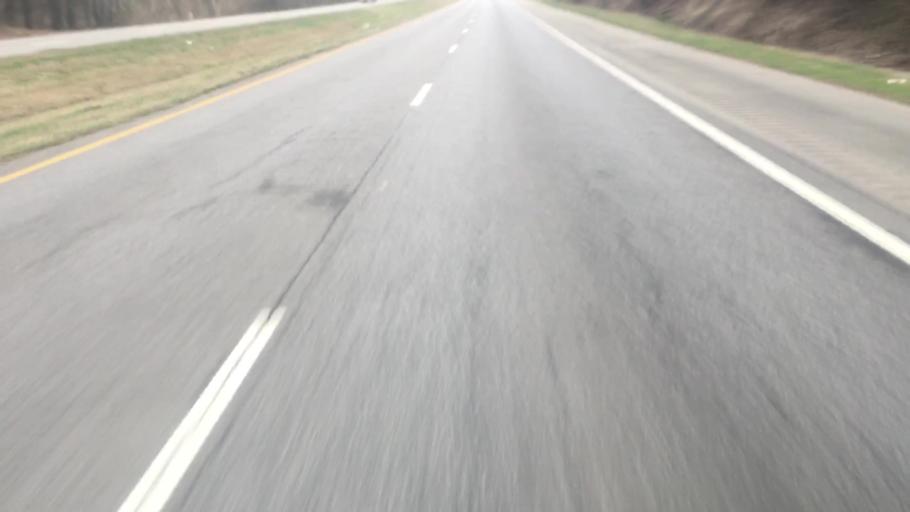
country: US
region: Alabama
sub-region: Jefferson County
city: Graysville
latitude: 33.6569
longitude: -86.9731
